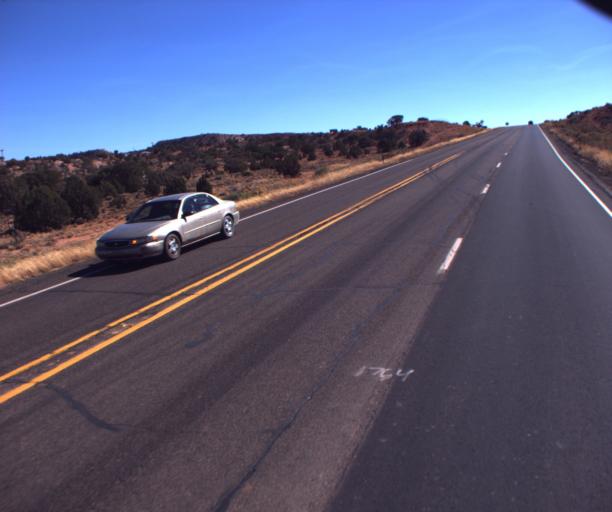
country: US
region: Arizona
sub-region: Apache County
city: Ganado
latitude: 35.7516
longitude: -109.6245
